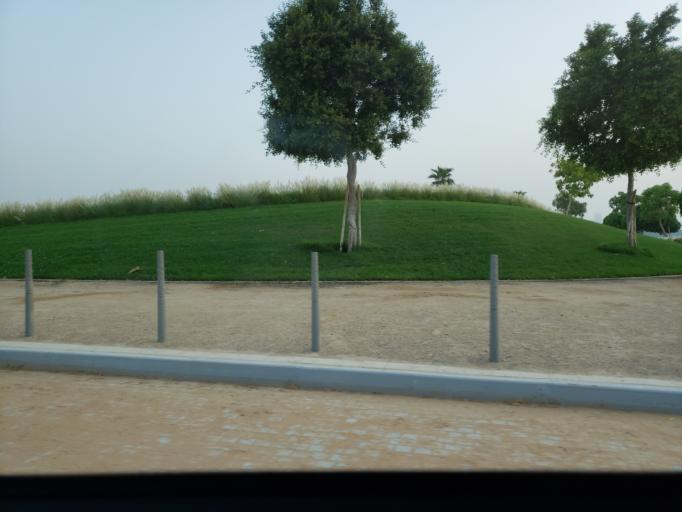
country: AE
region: Ajman
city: Ajman
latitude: 25.4347
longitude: 55.4641
